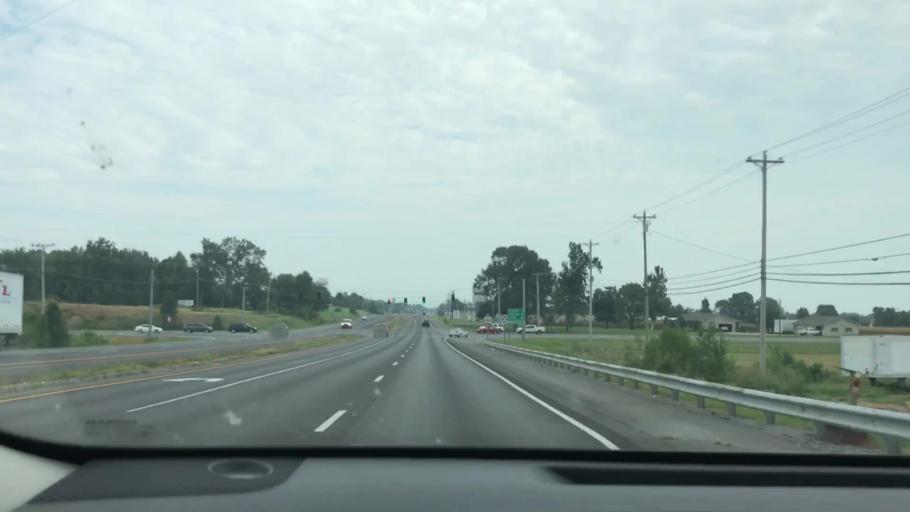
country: US
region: Kentucky
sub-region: Calloway County
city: Murray
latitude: 36.6509
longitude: -88.3070
